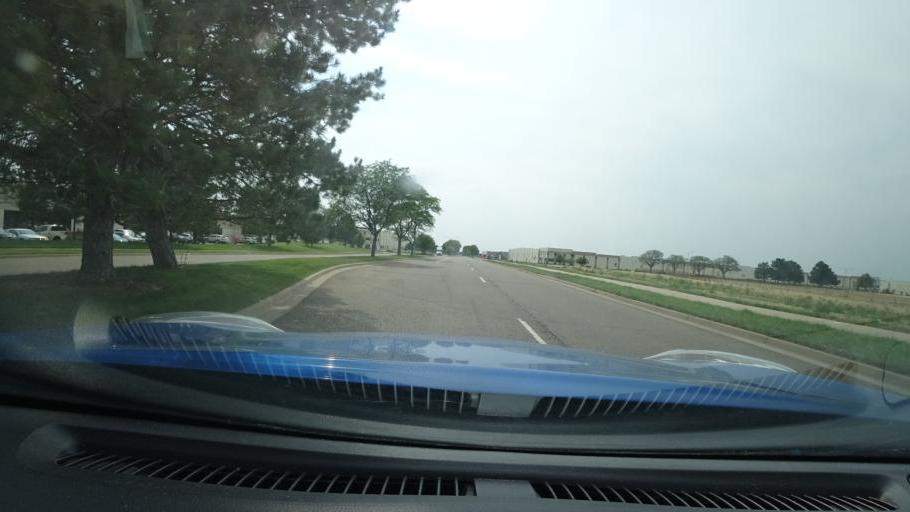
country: US
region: Colorado
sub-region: Adams County
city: Aurora
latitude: 39.7590
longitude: -104.7513
